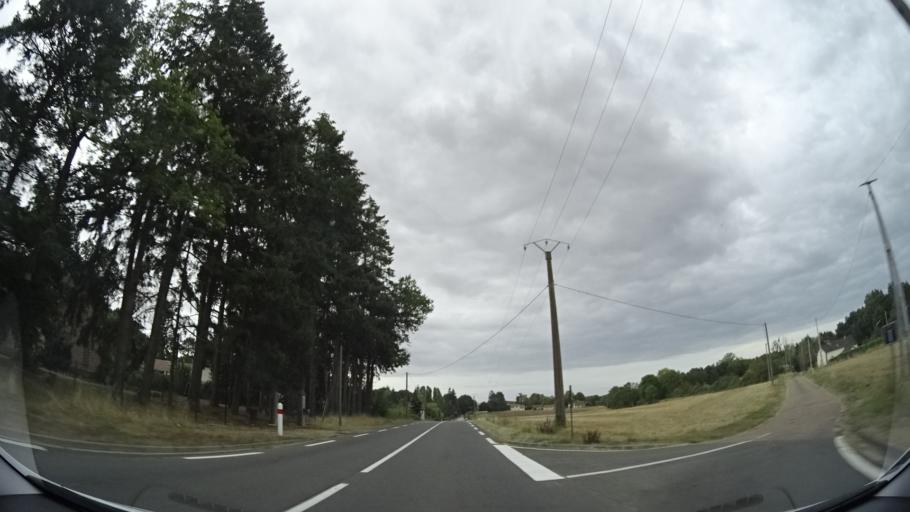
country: FR
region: Centre
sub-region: Departement du Loiret
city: Douchy
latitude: 47.9453
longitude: 3.0383
